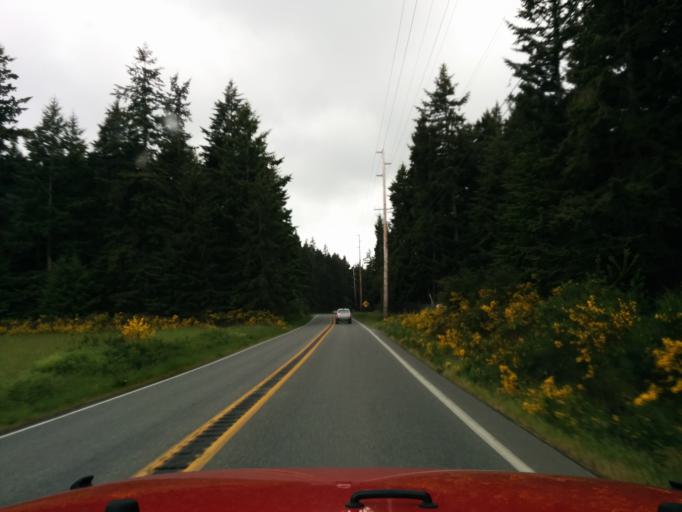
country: US
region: Washington
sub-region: Island County
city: Coupeville
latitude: 48.2078
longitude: -122.6444
